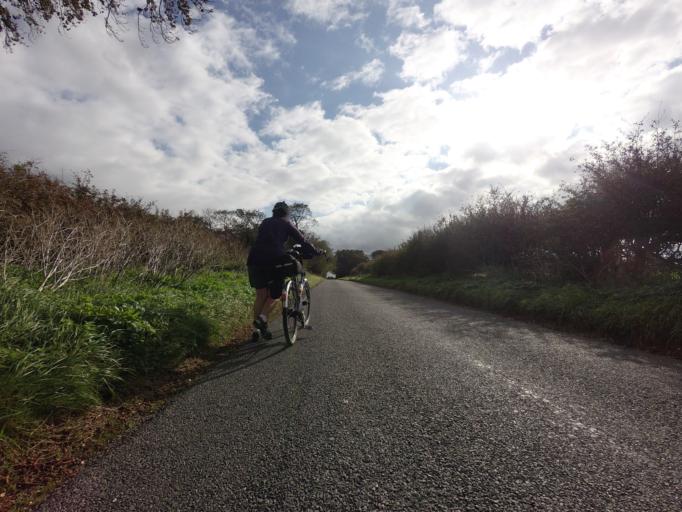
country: GB
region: England
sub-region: Norfolk
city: Heacham
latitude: 52.9193
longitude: 0.5420
